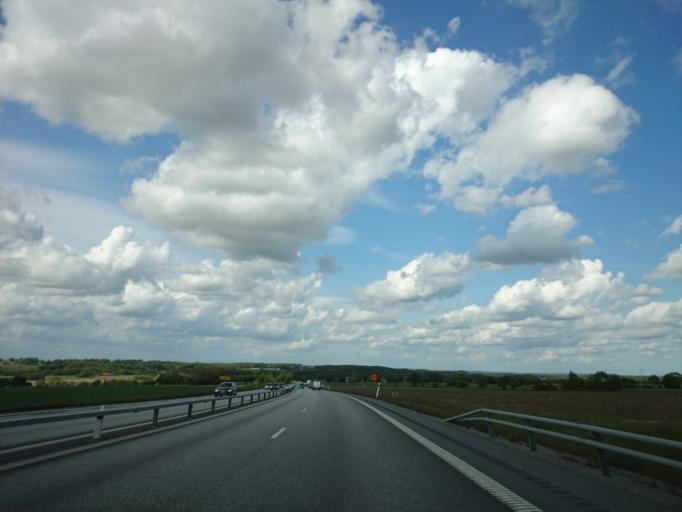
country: SE
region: Skane
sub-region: Hoors Kommun
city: Loberod
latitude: 55.7937
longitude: 13.4449
